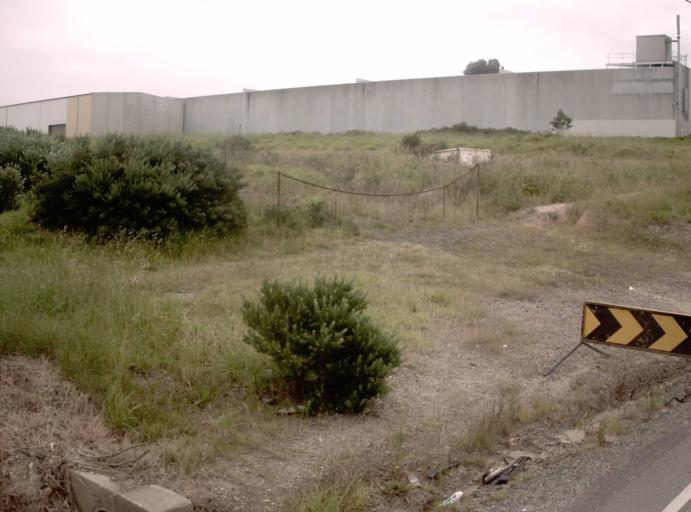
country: AU
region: Victoria
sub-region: Casey
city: Hallam
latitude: -38.0146
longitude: 145.2715
